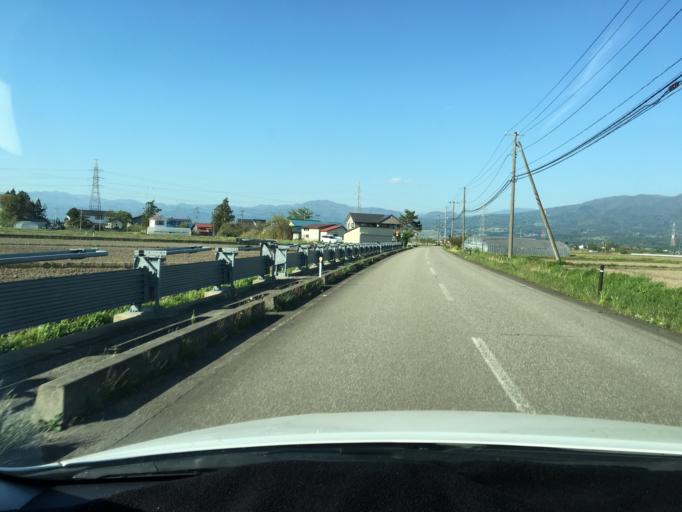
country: JP
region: Fukushima
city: Kitakata
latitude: 37.5725
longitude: 139.8768
